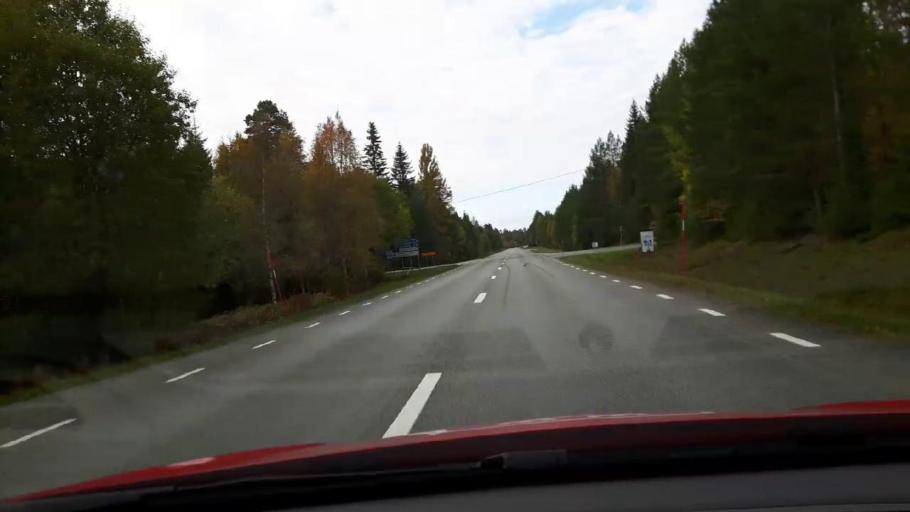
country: SE
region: Jaemtland
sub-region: Krokoms Kommun
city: Valla
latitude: 63.2575
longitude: 13.9880
